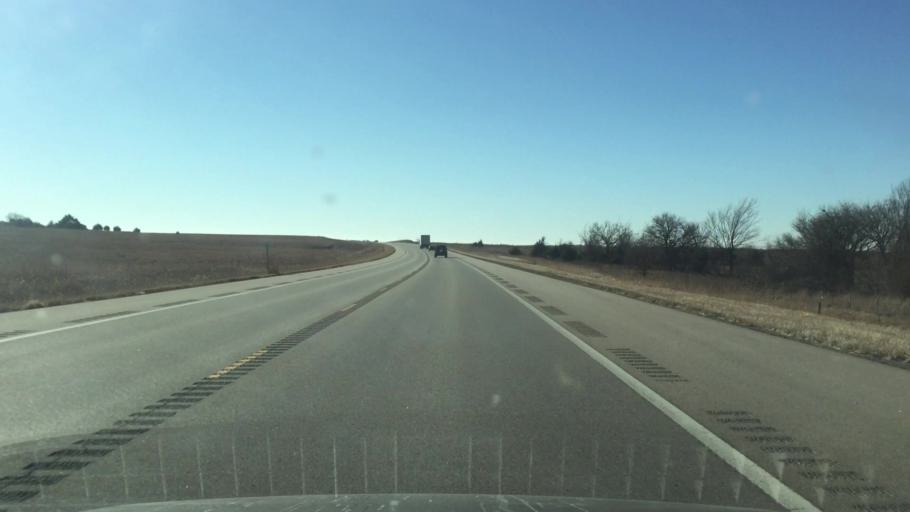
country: US
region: Kansas
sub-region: Allen County
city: Iola
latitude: 38.0653
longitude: -95.3799
